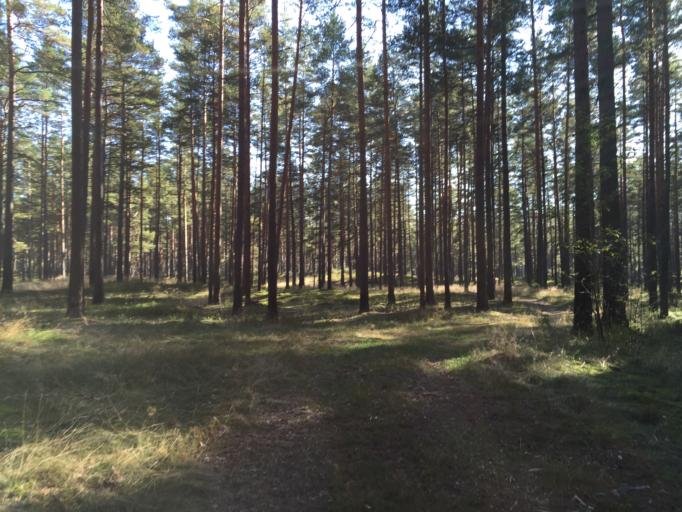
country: LV
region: Garkalne
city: Garkalne
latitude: 57.0245
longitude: 24.3642
